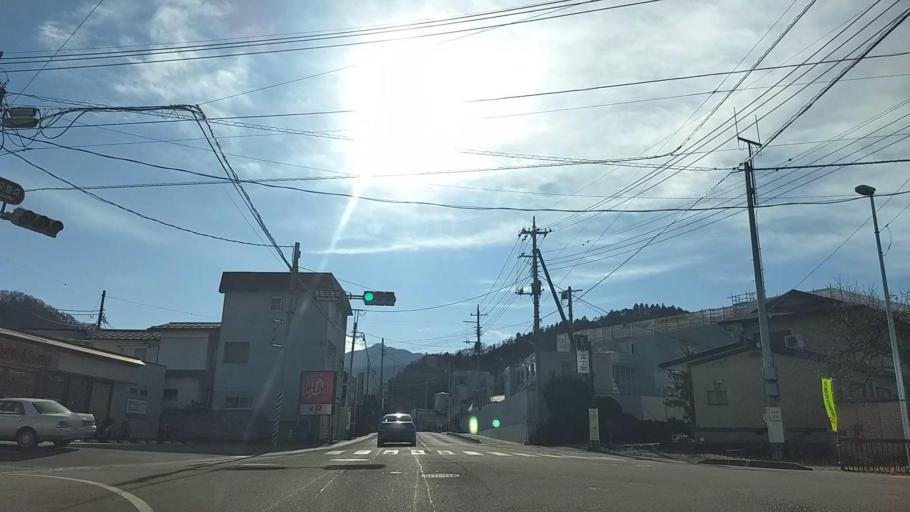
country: JP
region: Yamanashi
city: Otsuki
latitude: 35.5588
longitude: 138.9086
